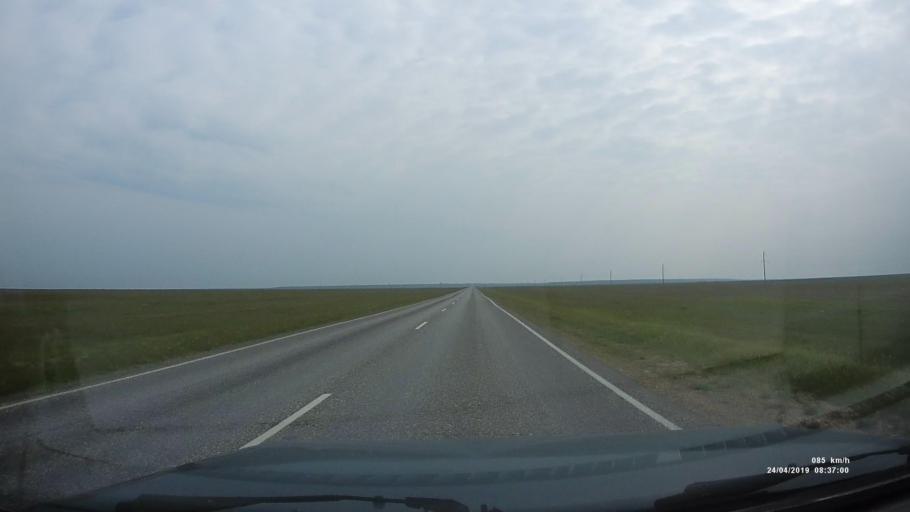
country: RU
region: Kalmykiya
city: Arshan'
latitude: 46.2077
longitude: 43.9437
